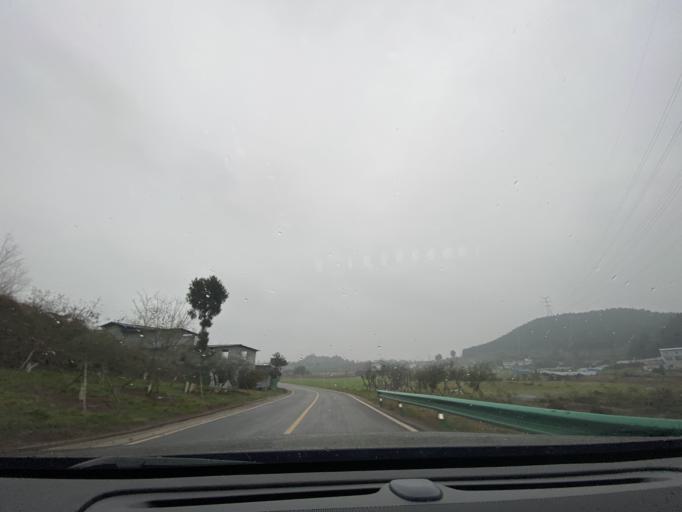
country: CN
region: Sichuan
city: Jiancheng
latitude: 30.3911
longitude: 104.6362
